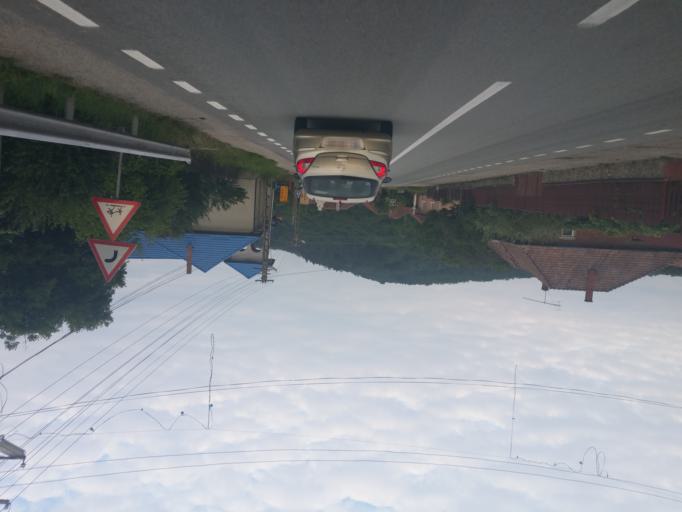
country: RO
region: Salaj
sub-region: Comuna Sanmihaiu Almasului
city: Sanmihaiu Almasului
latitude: 46.9566
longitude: 23.3444
